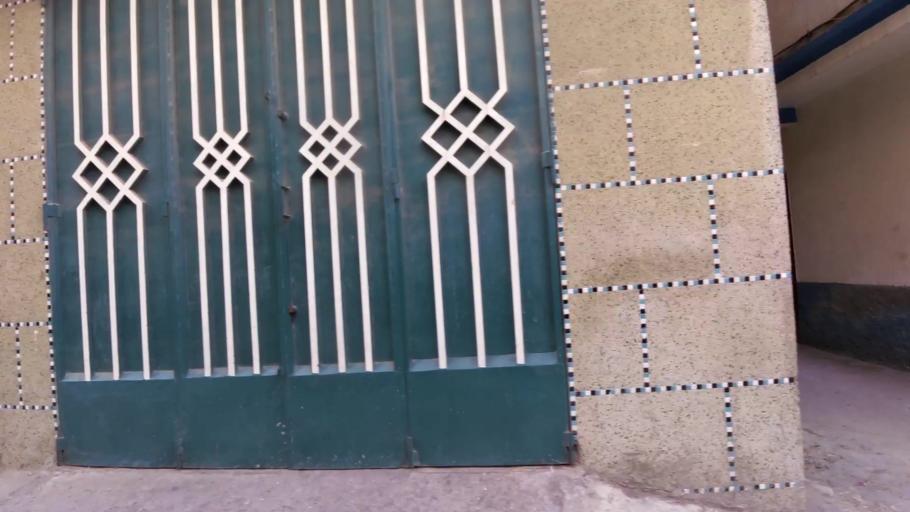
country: MA
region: Tanger-Tetouan
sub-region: Tanger-Assilah
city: Tangier
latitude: 35.7386
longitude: -5.8050
